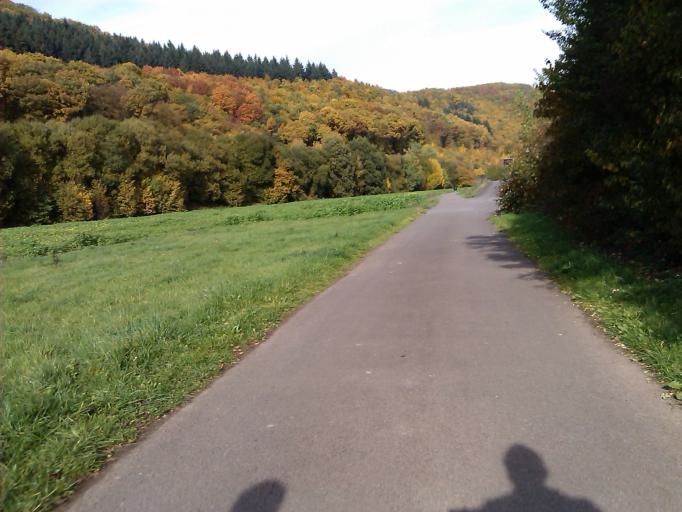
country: DE
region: Rheinland-Pfalz
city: Lauterecken
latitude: 49.6614
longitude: 7.5970
